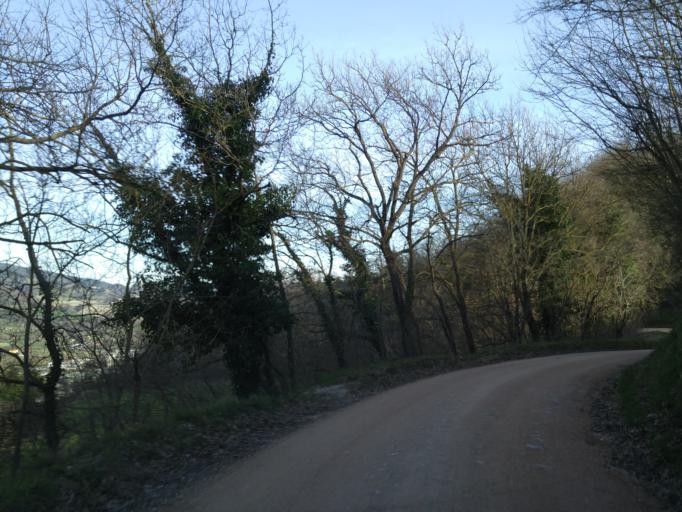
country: IT
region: The Marches
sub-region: Provincia di Pesaro e Urbino
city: Canavaccio
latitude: 43.6911
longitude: 12.6859
